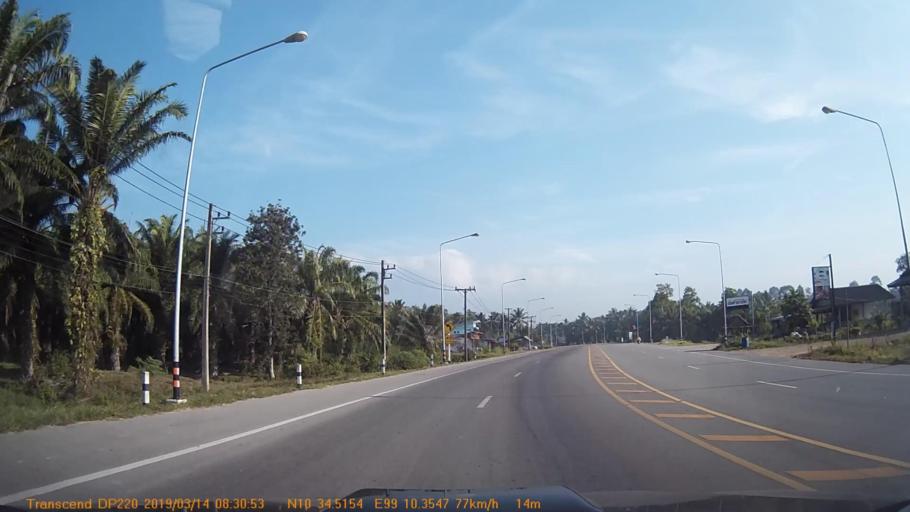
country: TH
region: Chumphon
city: Chumphon
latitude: 10.5756
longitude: 99.1725
